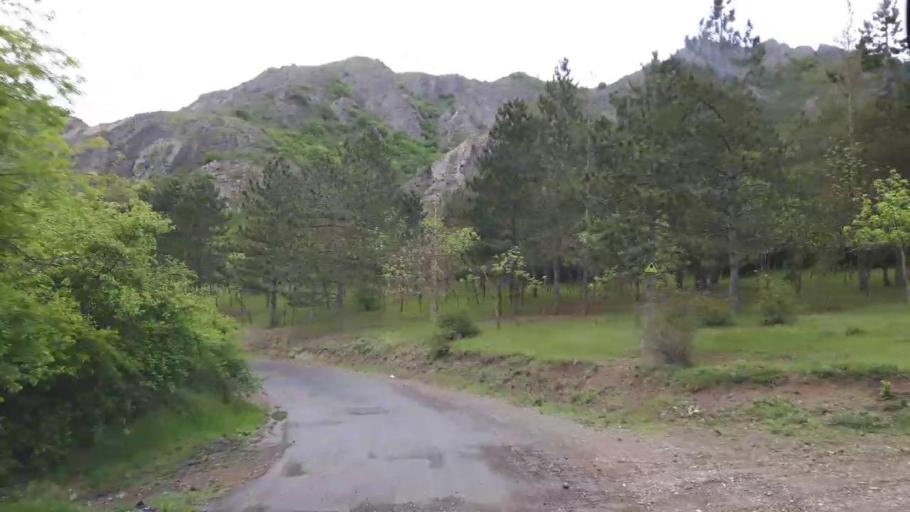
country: GE
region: Shida Kartli
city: Gori
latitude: 41.8990
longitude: 44.0485
